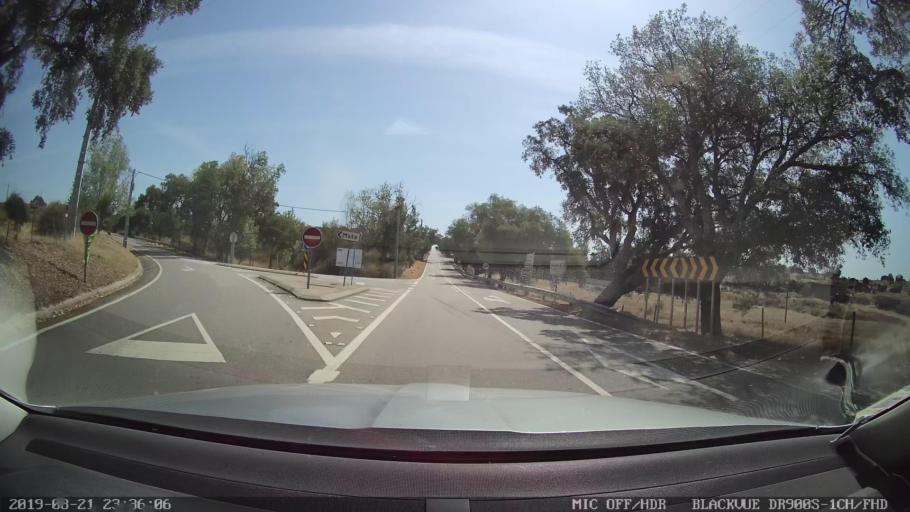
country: PT
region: Guarda
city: Alcains
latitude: 39.8772
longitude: -7.3802
